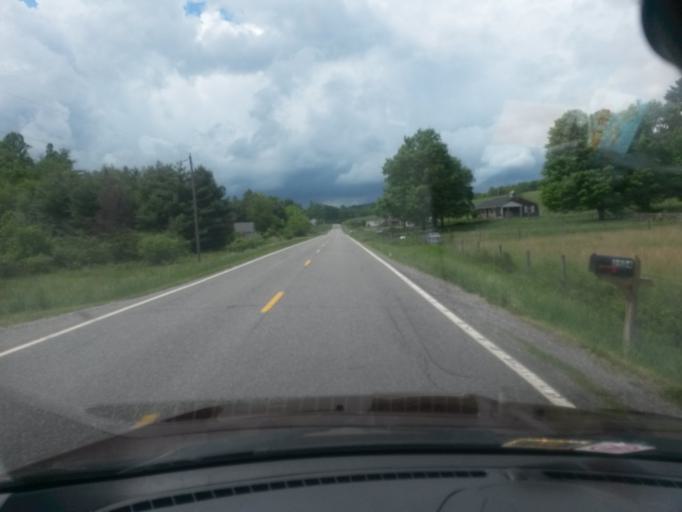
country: US
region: Virginia
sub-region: Floyd County
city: Floyd
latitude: 36.8535
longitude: -80.3187
